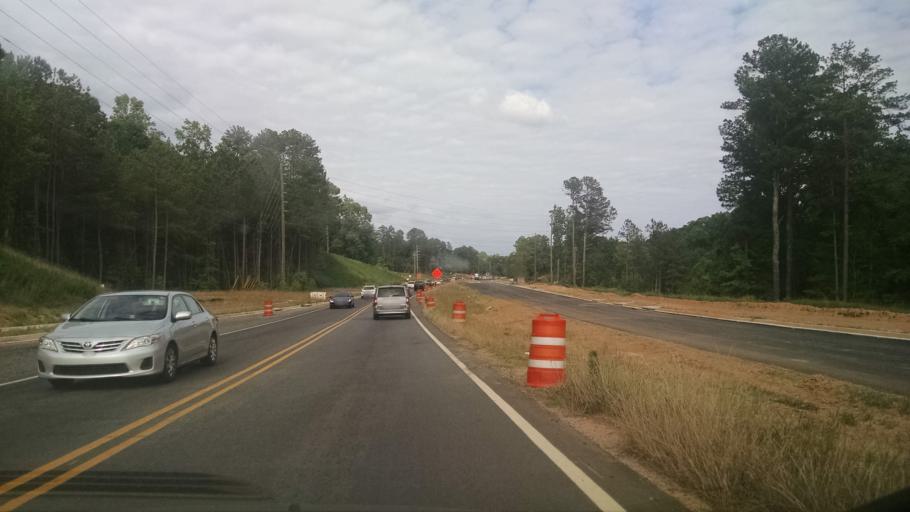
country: US
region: Georgia
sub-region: Gwinnett County
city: Sugar Hill
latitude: 34.1246
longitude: -84.0897
